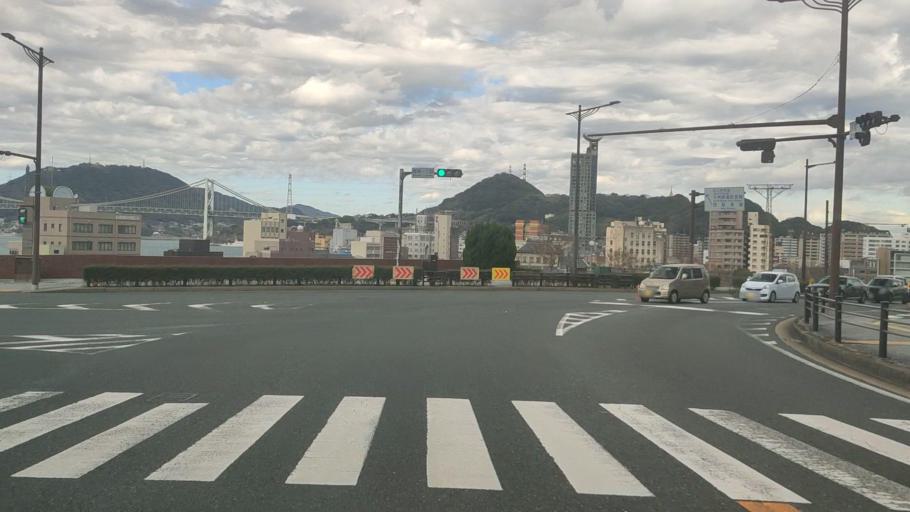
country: JP
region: Yamaguchi
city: Shimonoseki
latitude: 33.9418
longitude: 130.9594
